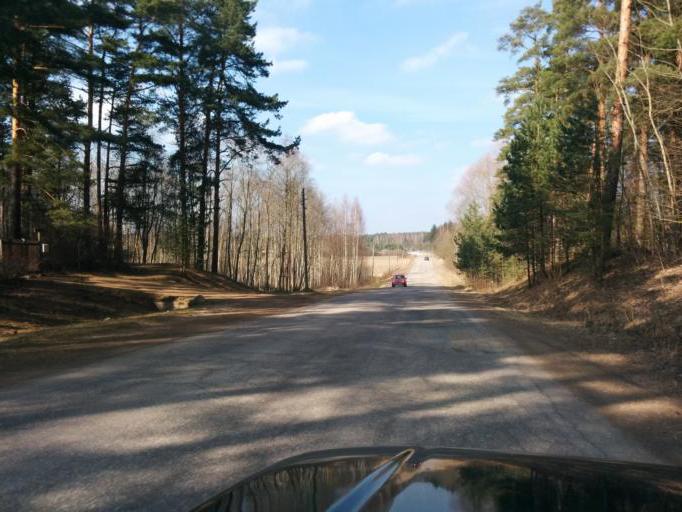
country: LV
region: Kekava
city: Kekava
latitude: 56.8468
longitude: 24.2433
